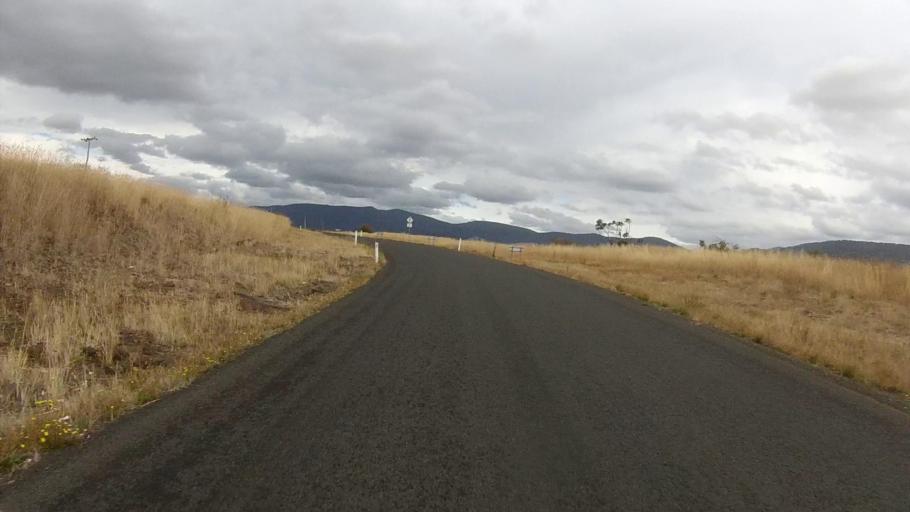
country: AU
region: Tasmania
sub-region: Northern Midlands
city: Evandale
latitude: -41.8184
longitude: 147.7544
